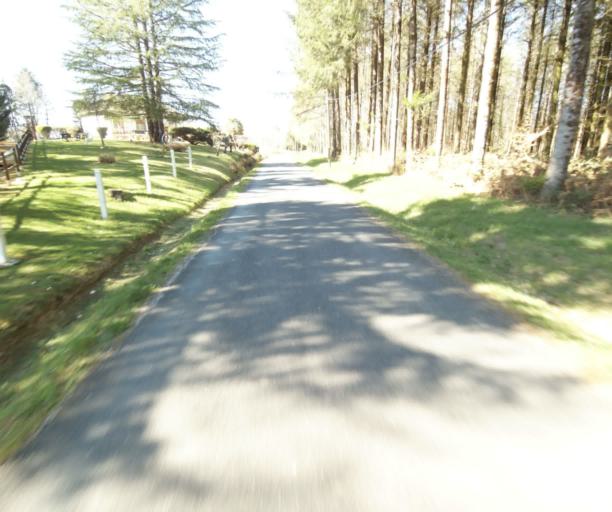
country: FR
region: Limousin
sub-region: Departement de la Correze
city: Chameyrat
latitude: 45.2827
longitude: 1.7142
